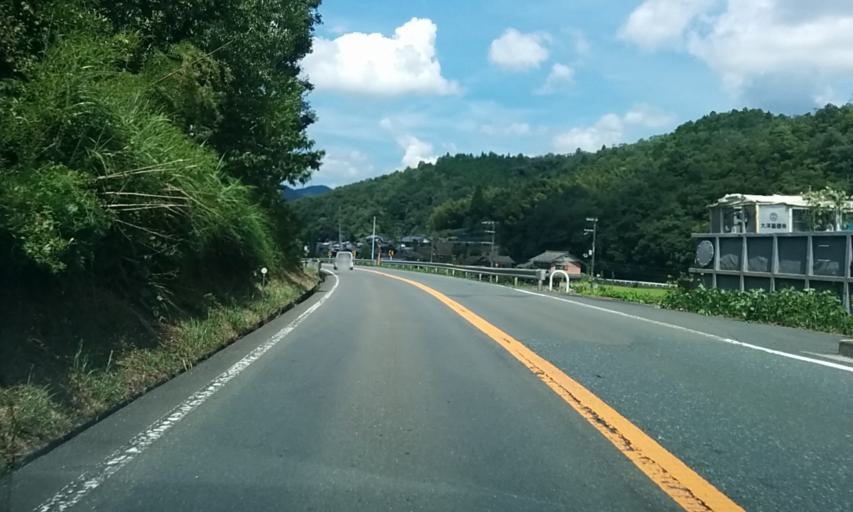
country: JP
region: Kyoto
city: Ayabe
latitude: 35.1828
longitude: 135.3446
